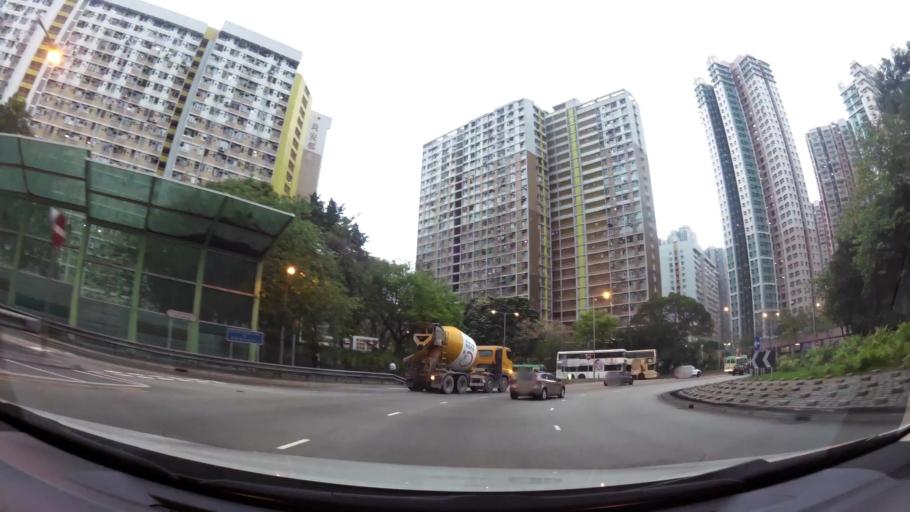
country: HK
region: Tsuen Wan
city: Tsuen Wan
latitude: 22.3599
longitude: 114.1023
